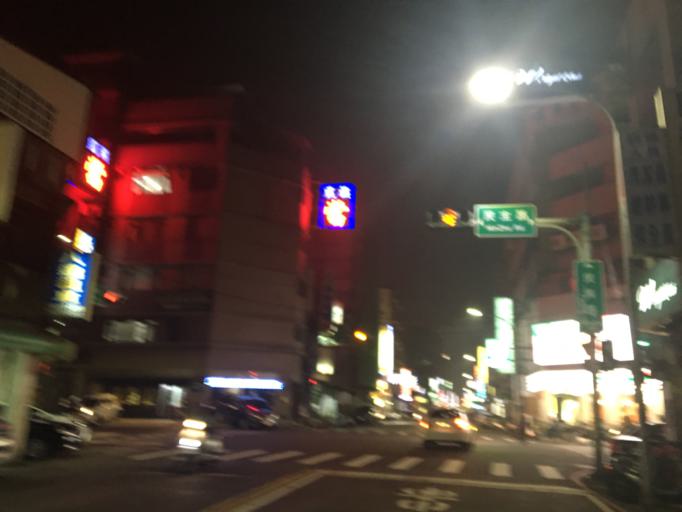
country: TW
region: Taiwan
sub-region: Hsinchu
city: Hsinchu
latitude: 24.8100
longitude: 120.9805
